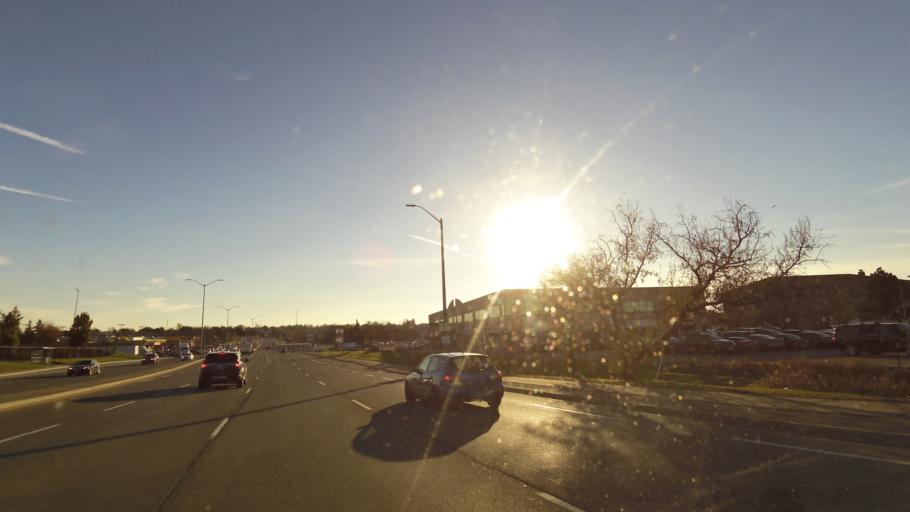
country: CA
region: Ontario
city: Mississauga
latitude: 43.5919
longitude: -79.7405
